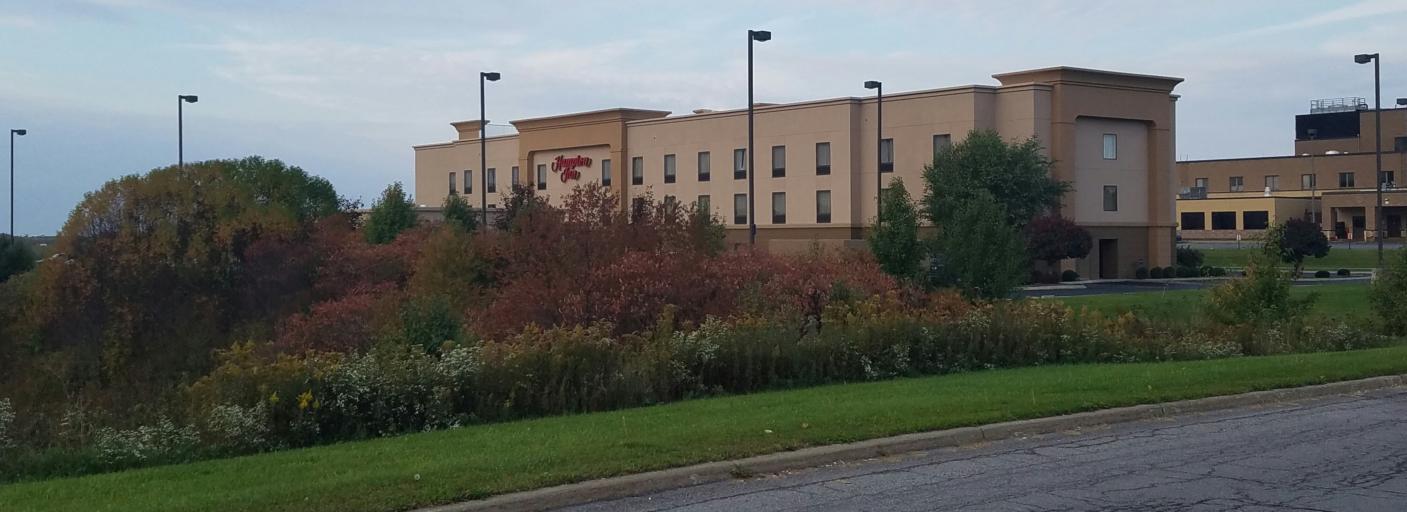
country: US
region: Pennsylvania
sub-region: Clarion County
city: Clarion
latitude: 41.1904
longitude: -79.3934
